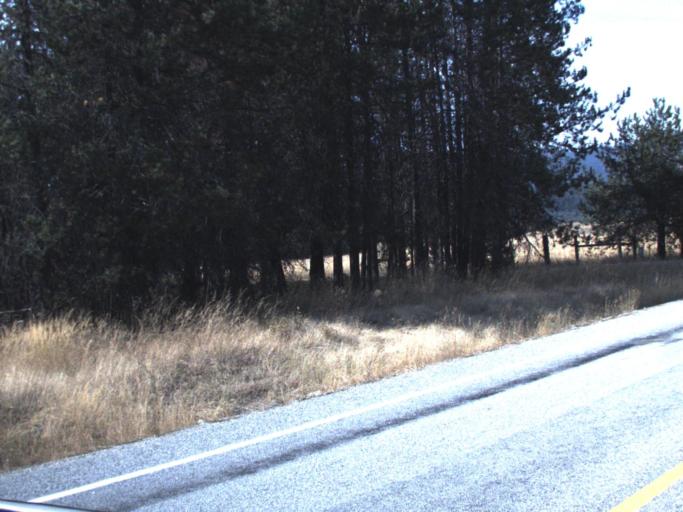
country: US
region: Washington
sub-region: Pend Oreille County
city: Newport
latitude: 48.1833
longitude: -117.3015
